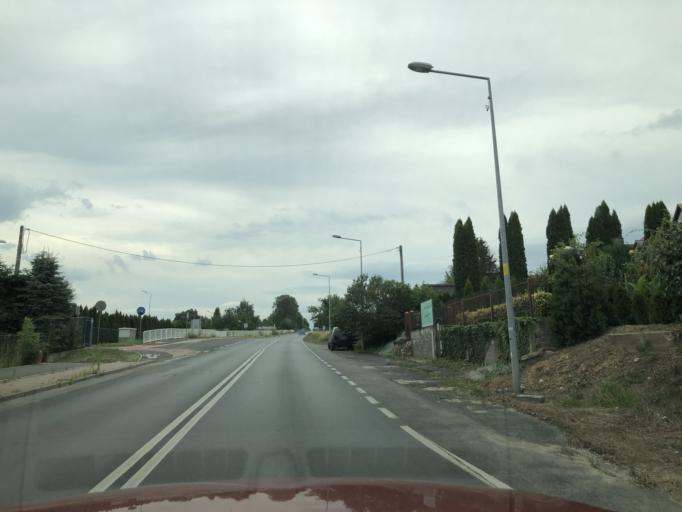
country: PL
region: Lower Silesian Voivodeship
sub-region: Powiat trzebnicki
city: Trzebnica
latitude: 51.2995
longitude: 17.0578
